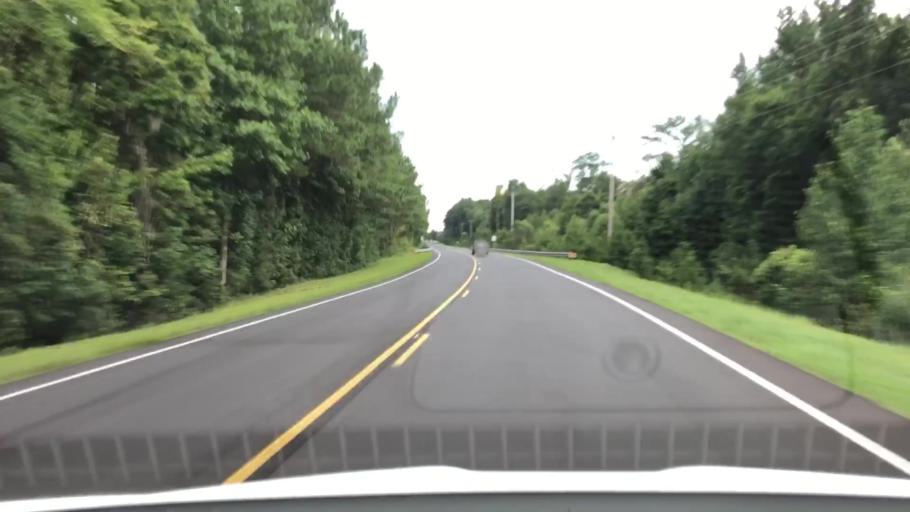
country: US
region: North Carolina
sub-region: Jones County
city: Maysville
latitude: 34.8706
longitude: -77.1953
